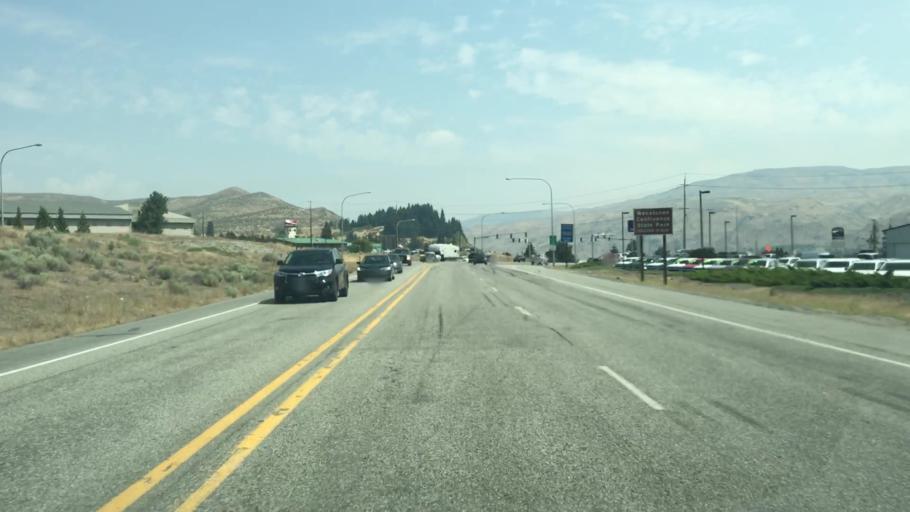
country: US
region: Washington
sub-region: Chelan County
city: Sunnyslope
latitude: 47.4680
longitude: -120.3376
